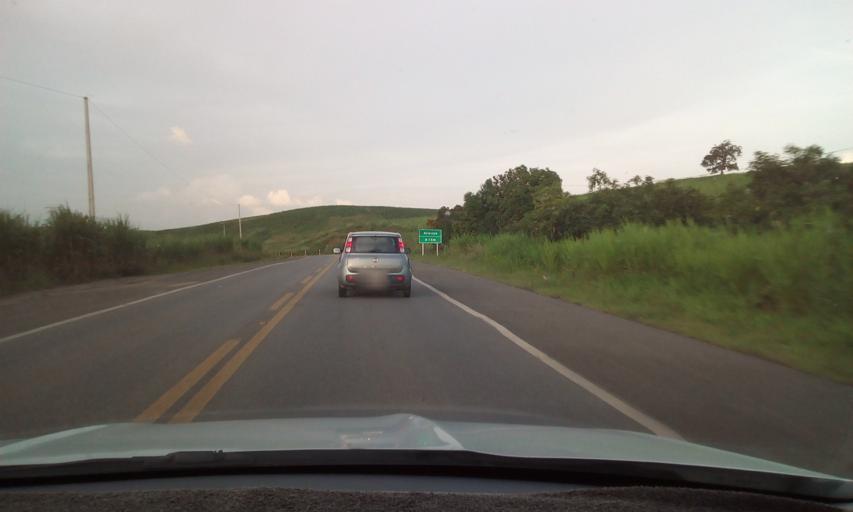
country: BR
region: Pernambuco
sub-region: Vicencia
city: Vicencia
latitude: -7.6261
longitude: -35.2431
